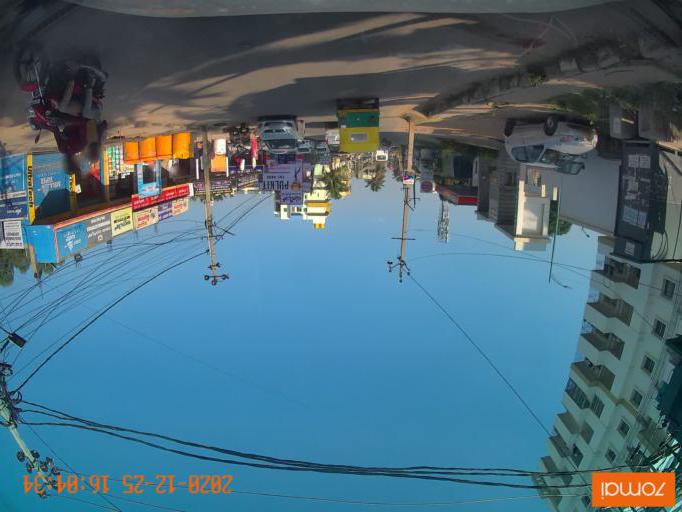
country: IN
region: Karnataka
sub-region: Bangalore Urban
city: Bangalore
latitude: 12.8865
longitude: 77.6255
